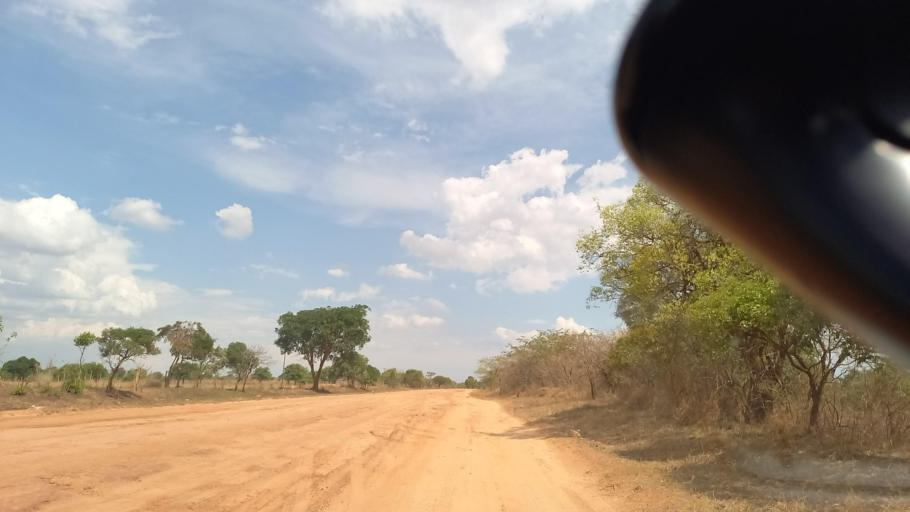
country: ZM
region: Lusaka
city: Kafue
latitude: -16.1174
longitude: 28.0352
